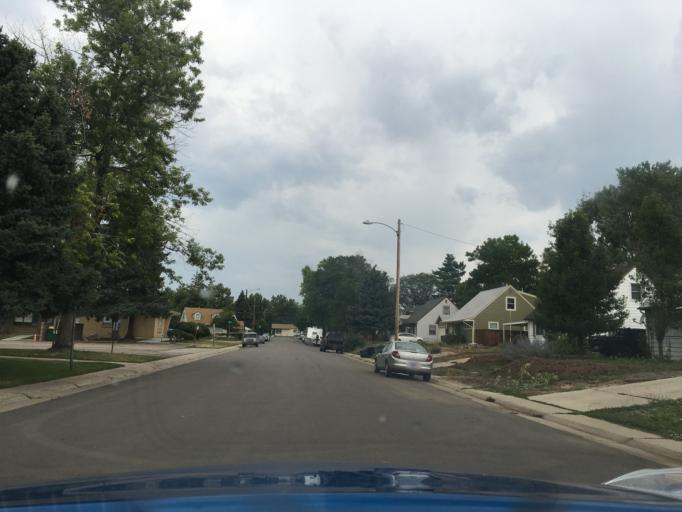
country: US
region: Colorado
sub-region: Arapahoe County
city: Sheridan
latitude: 39.6725
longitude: -105.0256
